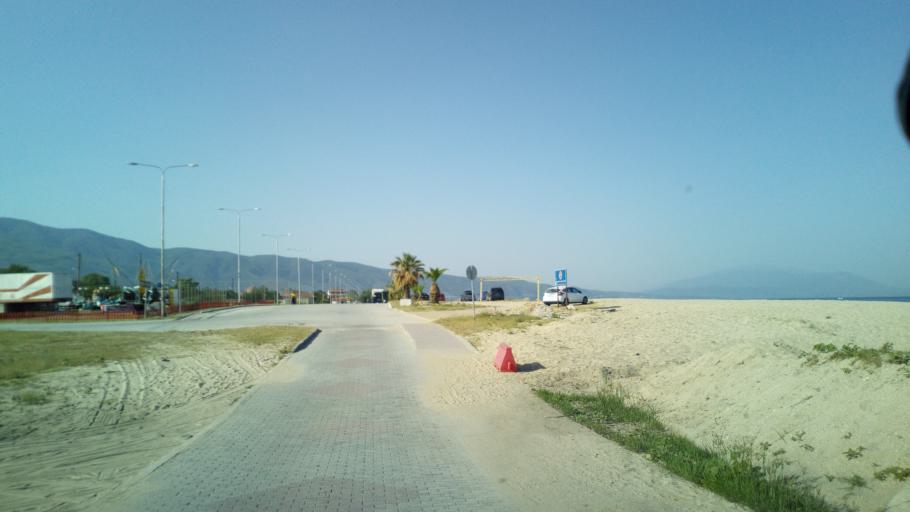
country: GR
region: Central Macedonia
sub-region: Nomos Thessalonikis
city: Nea Vrasna
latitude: 40.7119
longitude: 23.7047
